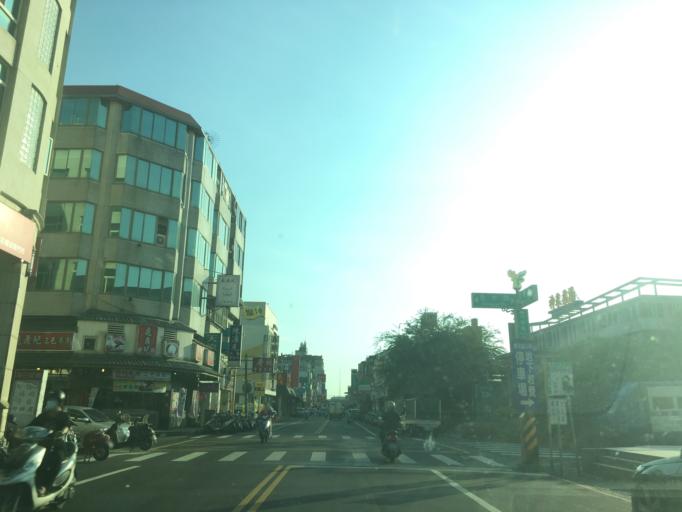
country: TW
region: Taiwan
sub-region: Changhua
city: Chang-hua
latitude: 24.0569
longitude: 120.4355
